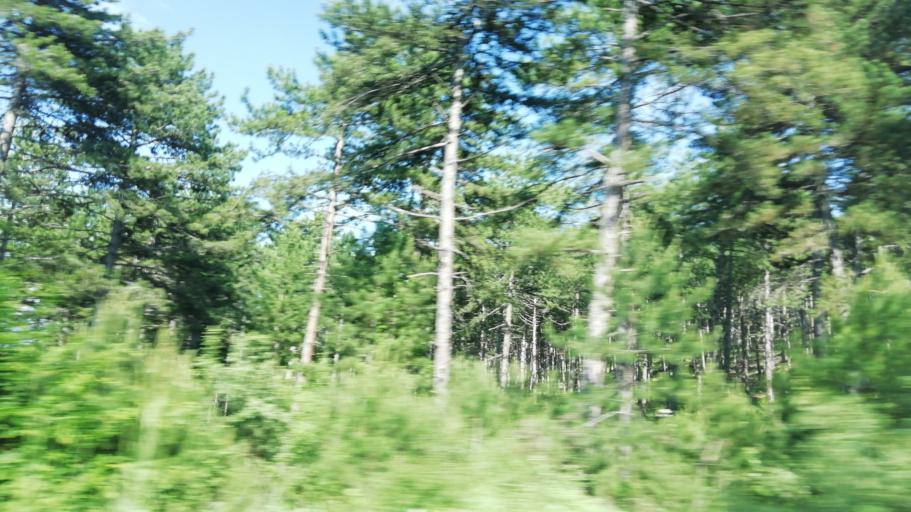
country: TR
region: Karabuk
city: Karabuk
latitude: 41.1121
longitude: 32.6067
